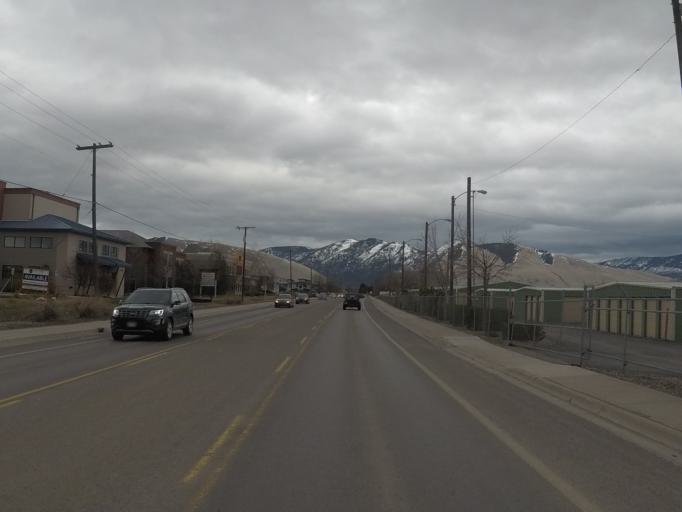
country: US
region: Montana
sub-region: Missoula County
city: Orchard Homes
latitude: 46.8836
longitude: -114.0335
